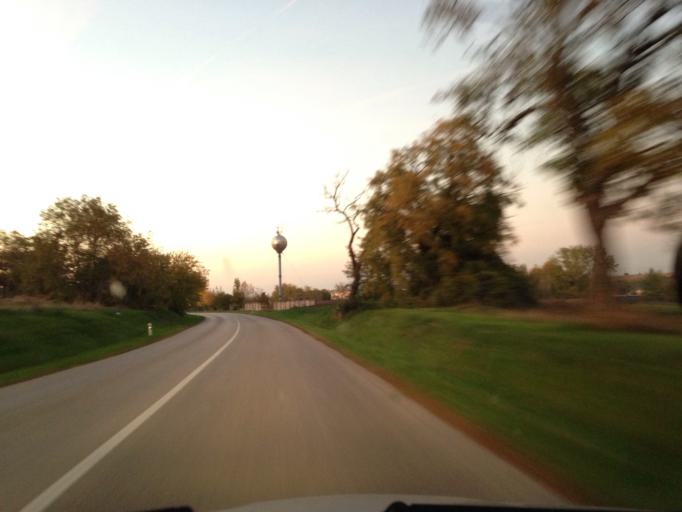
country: SK
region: Nitriansky
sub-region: Okres Komarno
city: Hurbanovo
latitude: 47.8603
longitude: 18.2738
